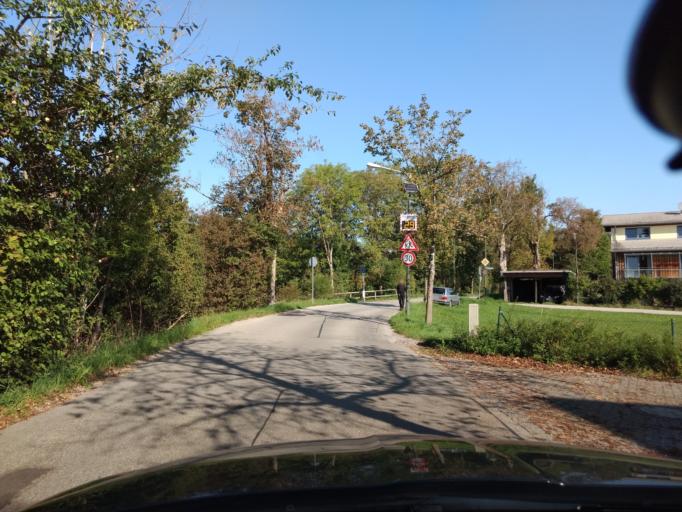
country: DE
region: Bavaria
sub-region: Upper Bavaria
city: Wolfratshausen
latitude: 47.9058
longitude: 11.4220
